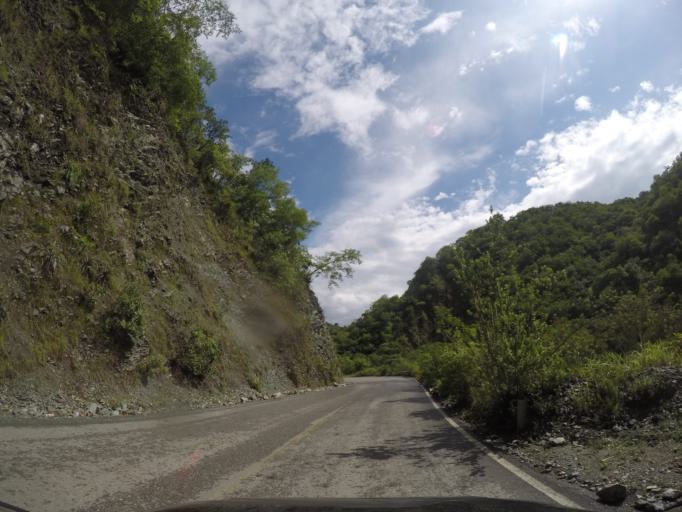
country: MX
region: Oaxaca
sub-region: San Jeronimo Coatlan
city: San Cristobal Honduras
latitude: 16.3665
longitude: -97.0881
